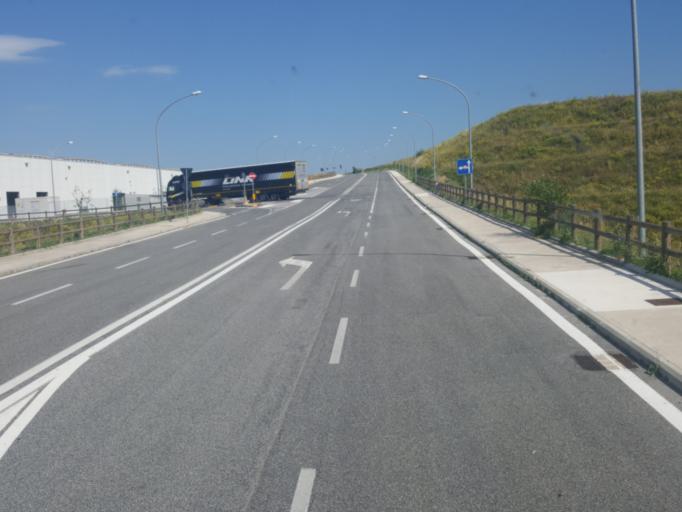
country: IT
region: Latium
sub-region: Citta metropolitana di Roma Capitale
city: Fiano Romano
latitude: 42.1676
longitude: 12.6495
